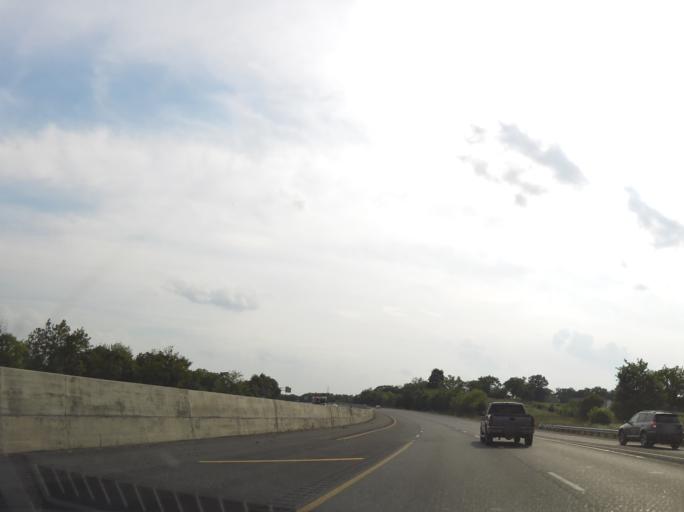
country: US
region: Maryland
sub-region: Washington County
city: Williamsport
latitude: 39.5798
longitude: -77.8772
